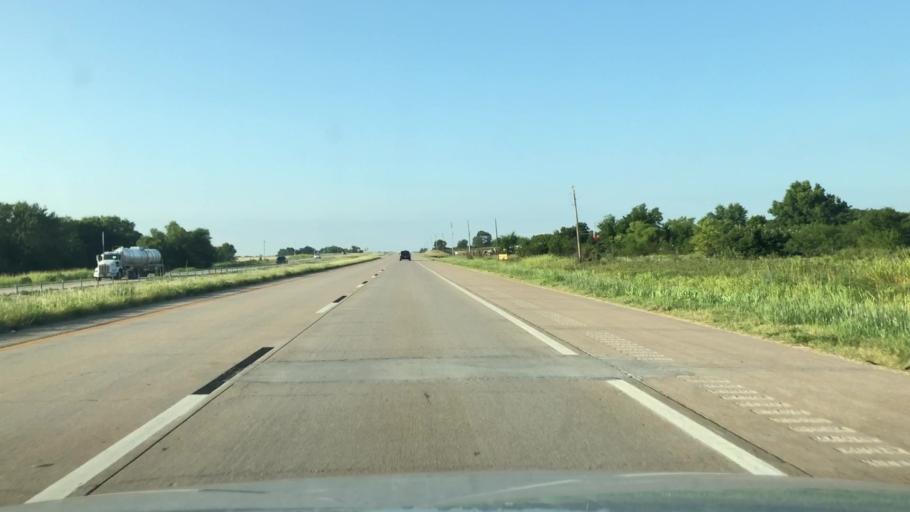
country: US
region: Oklahoma
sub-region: Osage County
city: Skiatook
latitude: 36.4699
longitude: -95.9207
